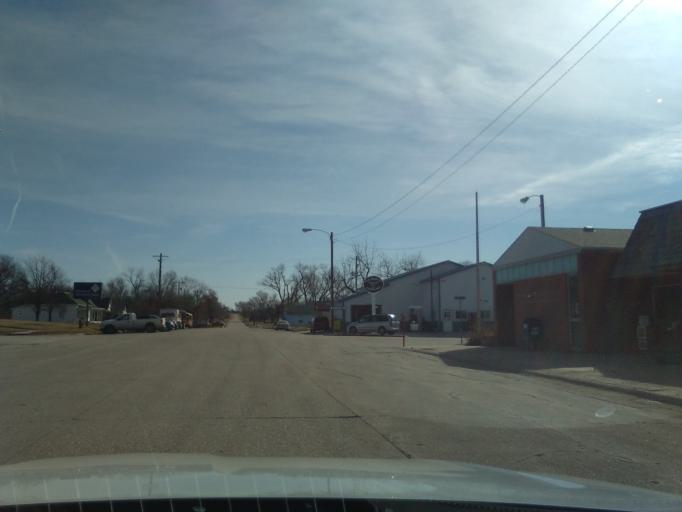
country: US
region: Nebraska
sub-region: Saline County
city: Friend
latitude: 40.7785
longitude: -97.2806
